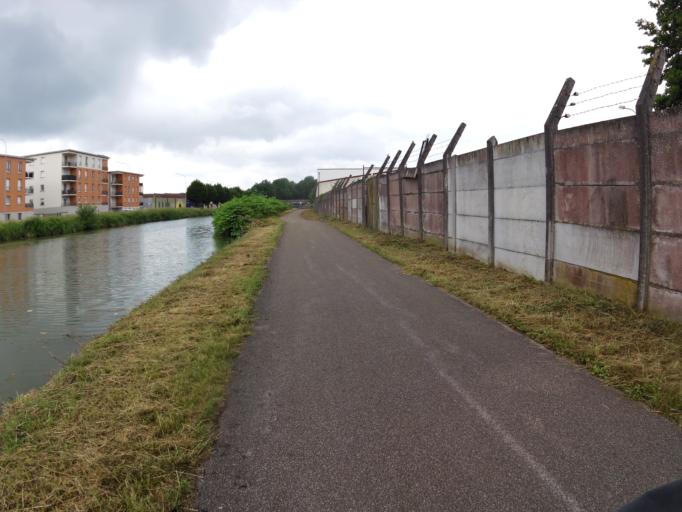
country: FR
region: Champagne-Ardenne
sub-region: Departement de la Haute-Marne
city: Saint-Dizier
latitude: 48.6425
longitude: 4.9386
